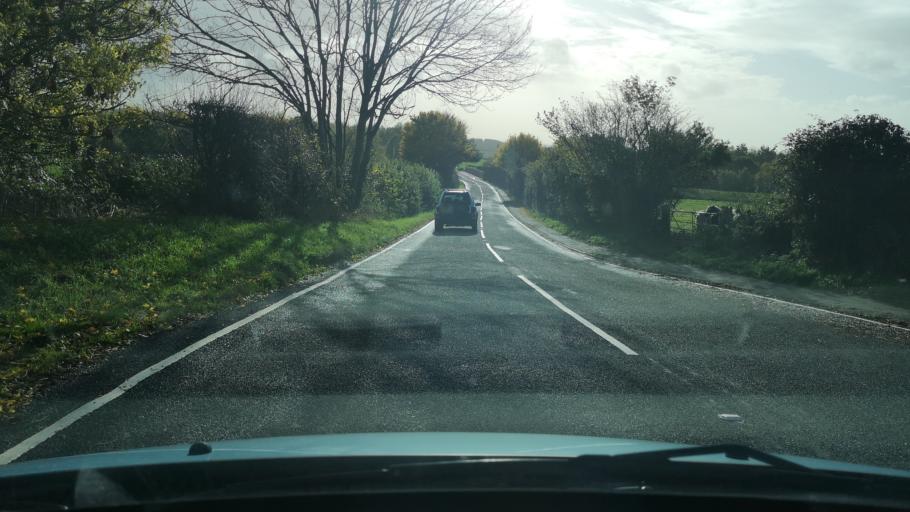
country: GB
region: England
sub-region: City and Borough of Wakefield
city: Crofton
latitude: 53.6504
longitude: -1.4178
